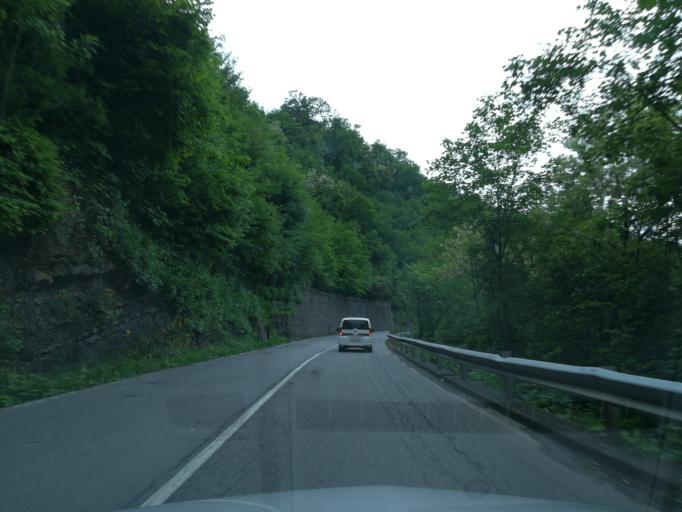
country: IT
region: Lombardy
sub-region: Provincia di Bergamo
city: Camoneone
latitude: 45.7892
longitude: 9.5687
